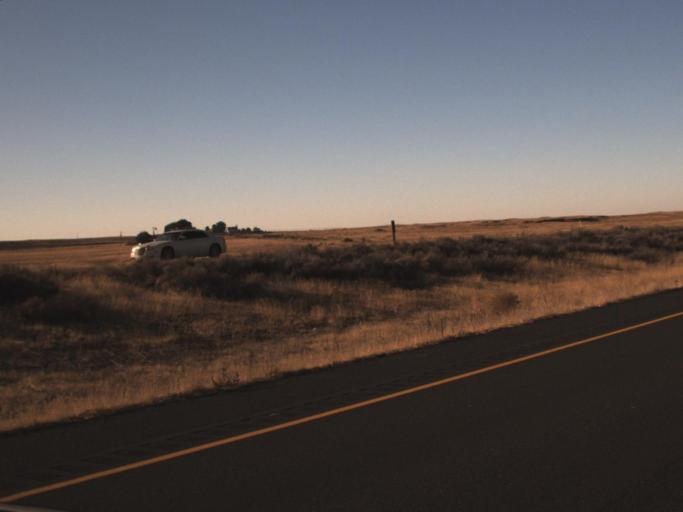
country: US
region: Washington
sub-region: Franklin County
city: Connell
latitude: 46.6326
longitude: -118.8784
